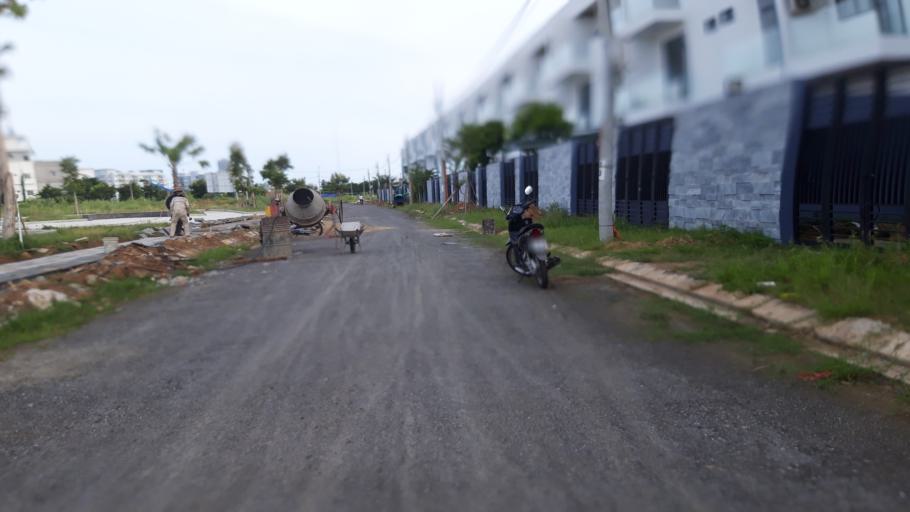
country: VN
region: Da Nang
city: Da Nang
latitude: 16.0923
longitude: 108.2262
